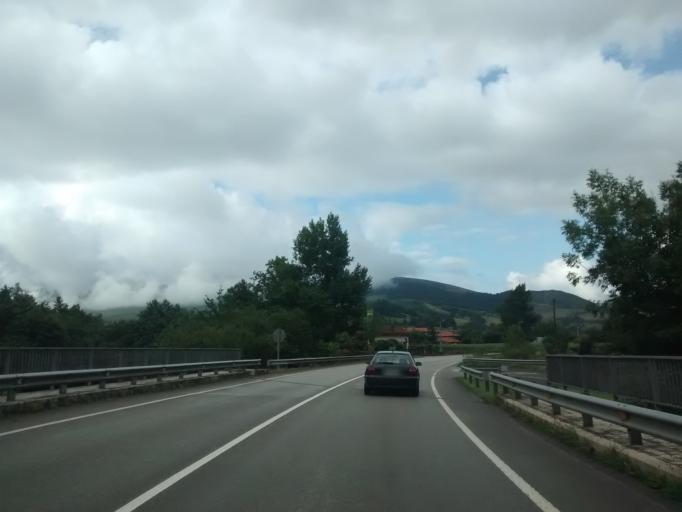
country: ES
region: Cantabria
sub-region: Provincia de Cantabria
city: Ruente
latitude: 43.2719
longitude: -4.2458
